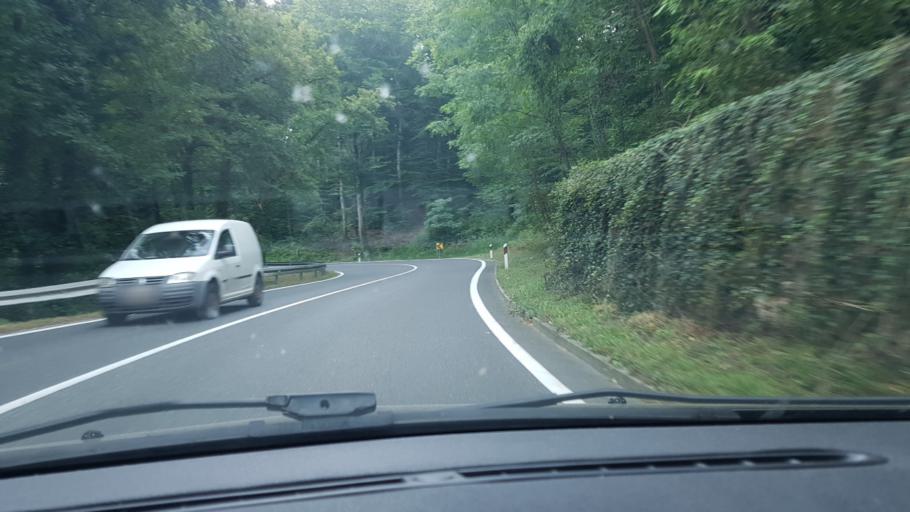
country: HR
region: Krapinsko-Zagorska
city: Mihovljan
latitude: 46.1489
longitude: 15.9484
